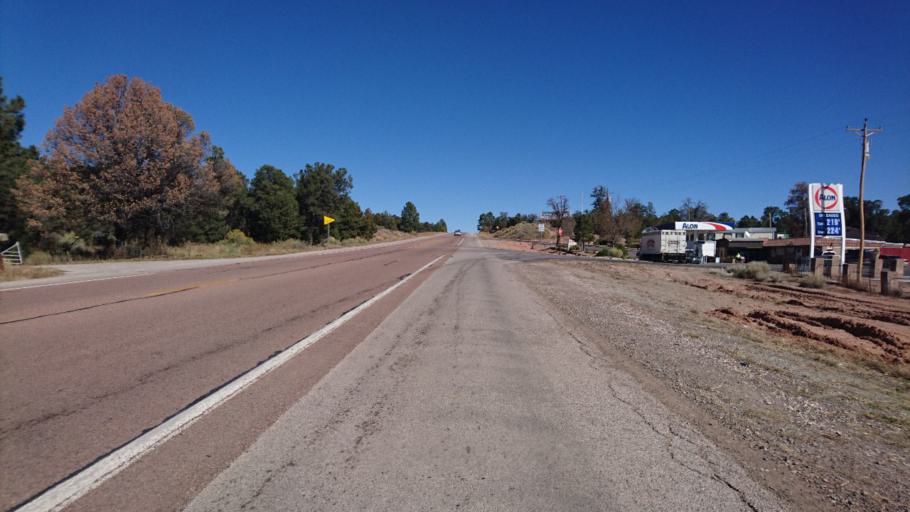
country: US
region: New Mexico
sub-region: McKinley County
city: Black Rock
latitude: 35.2400
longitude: -108.7627
